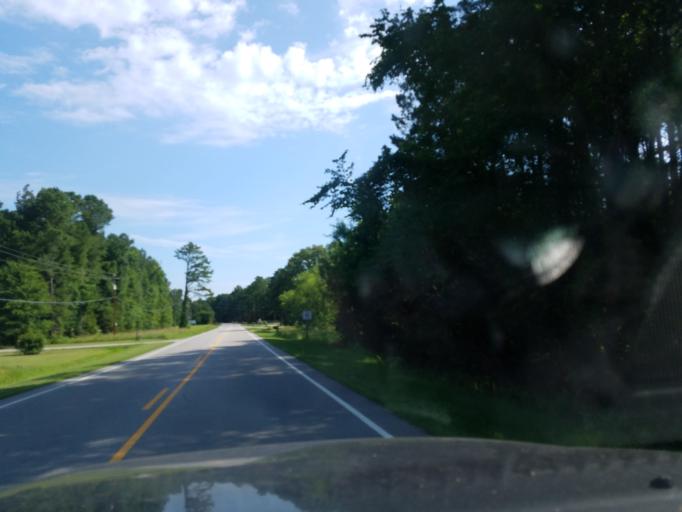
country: US
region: North Carolina
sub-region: Vance County
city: Henderson
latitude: 36.3606
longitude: -78.4193
